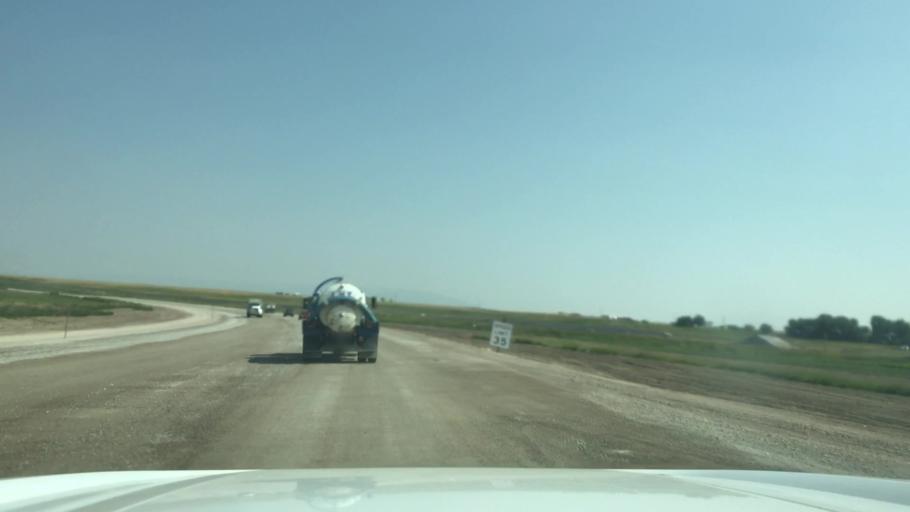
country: US
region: Montana
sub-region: Judith Basin County
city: Stanford
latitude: 47.0052
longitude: -109.8692
